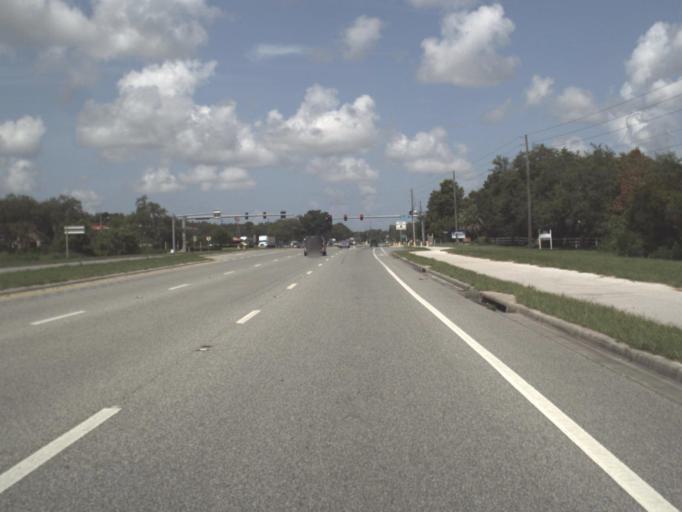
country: US
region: Florida
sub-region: Pasco County
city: Shady Hills
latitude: 28.3309
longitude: -82.5570
